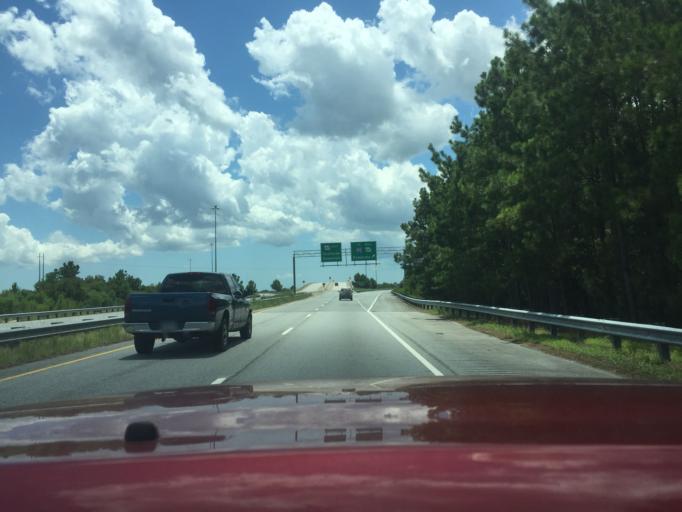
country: US
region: Georgia
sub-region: Chatham County
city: Georgetown
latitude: 31.9887
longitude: -81.1997
